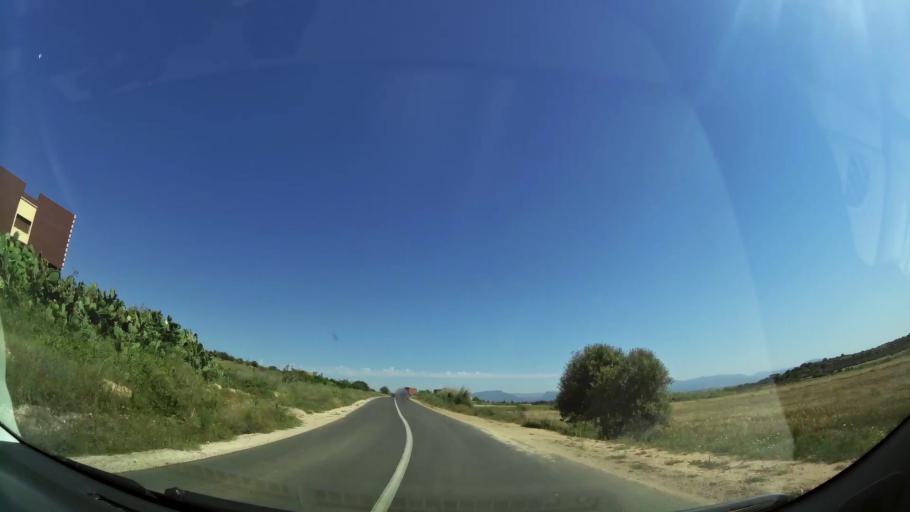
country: MA
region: Oriental
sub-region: Berkane-Taourirt
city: Madagh
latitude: 35.0450
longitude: -2.4289
